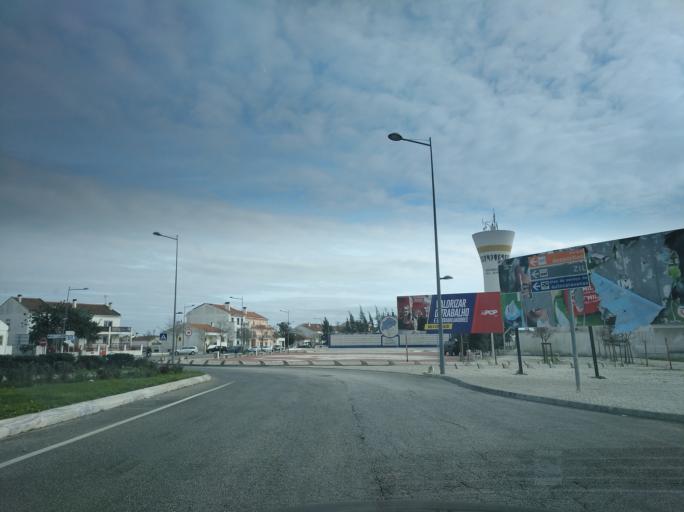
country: PT
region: Setubal
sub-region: Grandola
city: Grandola
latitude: 38.1842
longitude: -8.5682
